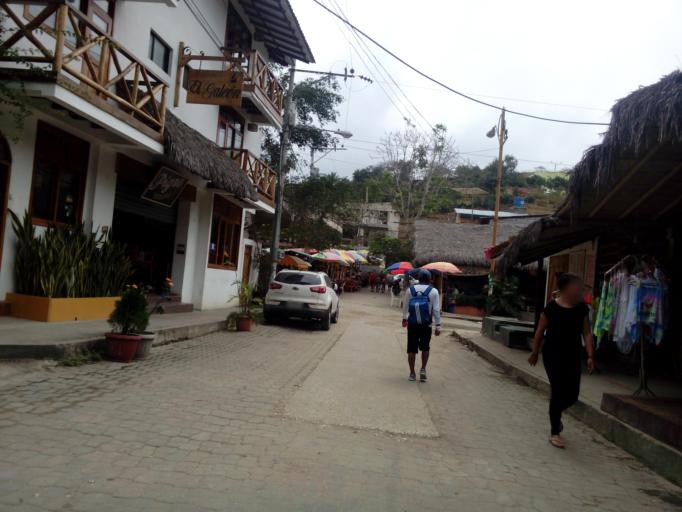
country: EC
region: Santa Elena
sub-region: Canton Santa Elena
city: Santa Elena
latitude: -1.8260
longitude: -80.7529
